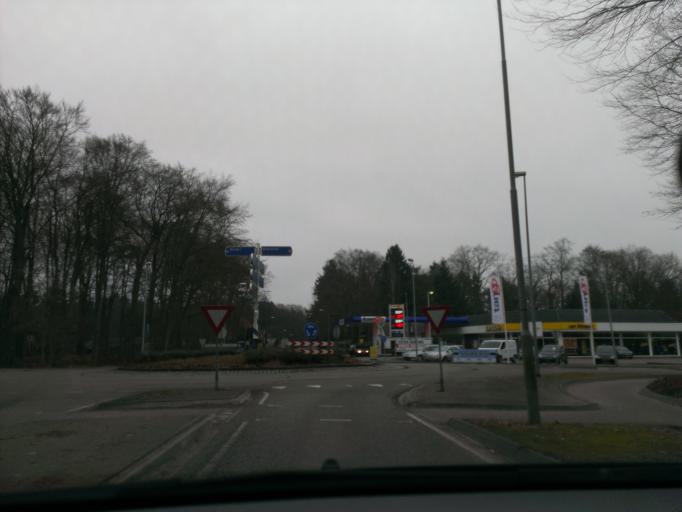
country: NL
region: Gelderland
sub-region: Gemeente Hattem
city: Hattem
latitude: 52.4327
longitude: 6.0678
